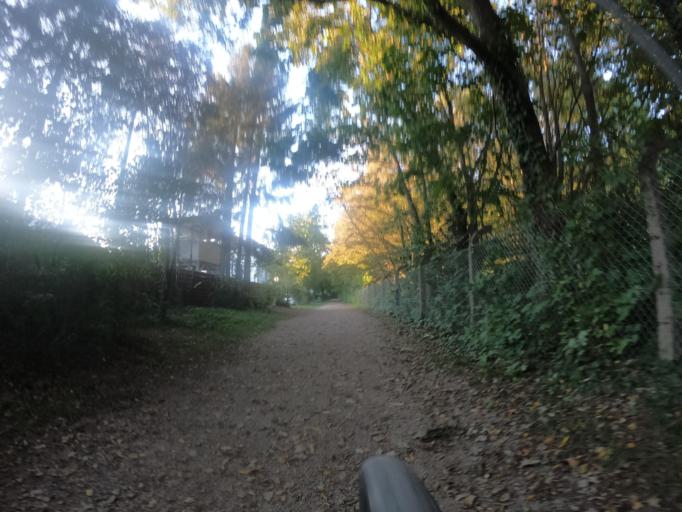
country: DE
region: Bavaria
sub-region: Upper Bavaria
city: Fuerstenfeldbruck
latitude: 48.1902
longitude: 11.2600
